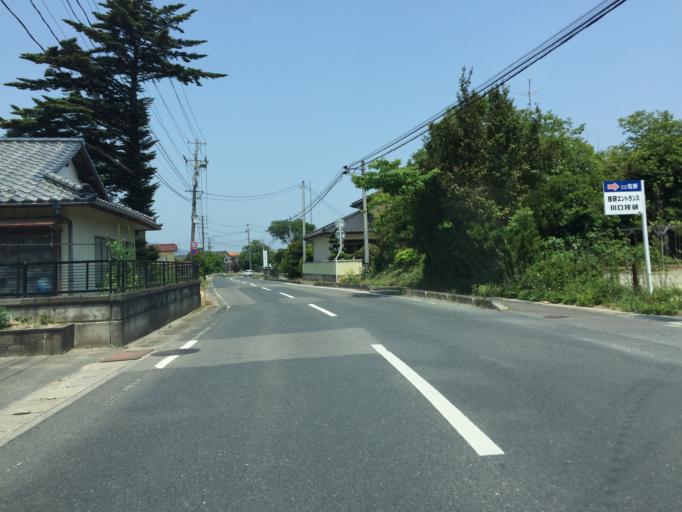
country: JP
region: Miyagi
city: Marumori
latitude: 37.8228
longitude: 140.8953
